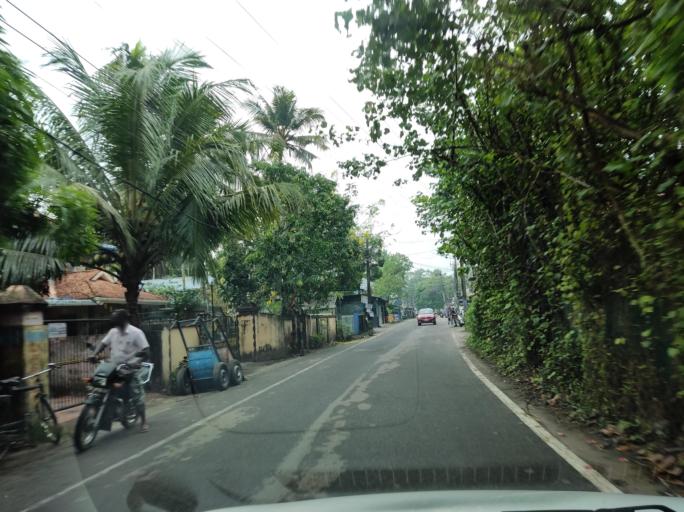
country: IN
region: Kerala
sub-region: Alappuzha
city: Kayankulam
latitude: 9.2445
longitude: 76.4532
